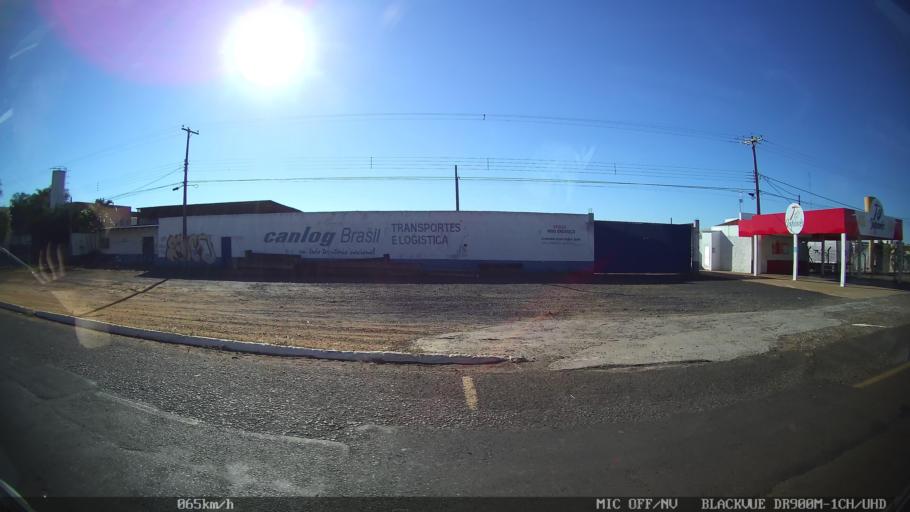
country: BR
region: Sao Paulo
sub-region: Franca
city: Franca
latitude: -20.5630
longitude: -47.3946
